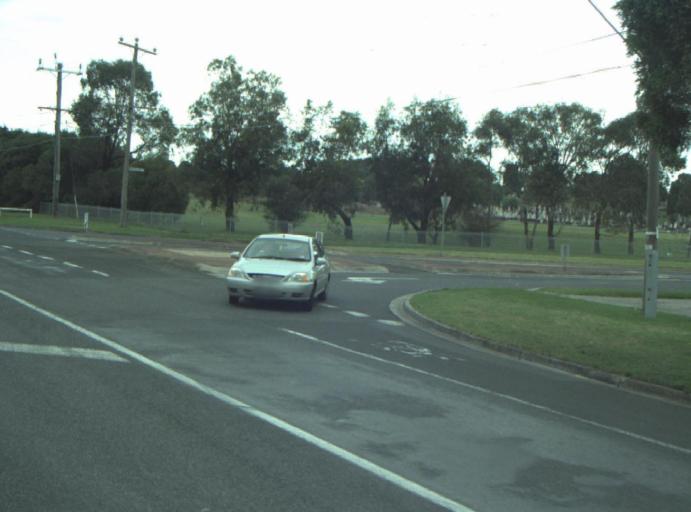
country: AU
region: Victoria
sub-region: Greater Geelong
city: East Geelong
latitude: -38.1611
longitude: 144.3860
